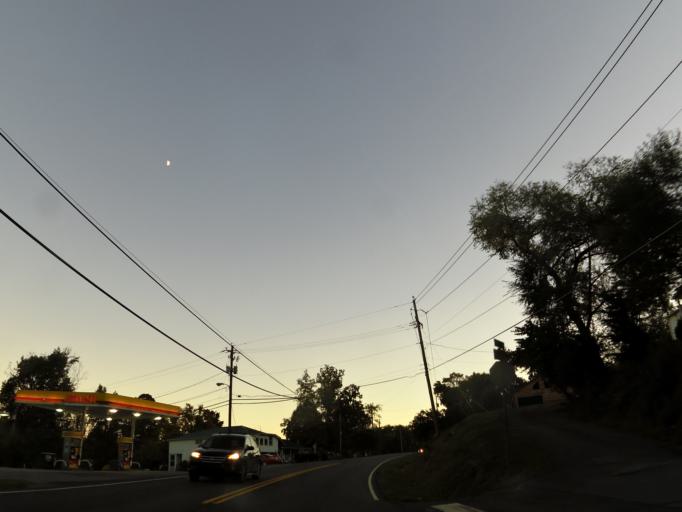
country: US
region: Tennessee
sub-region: Union County
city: Condon
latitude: 36.1099
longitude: -83.8525
